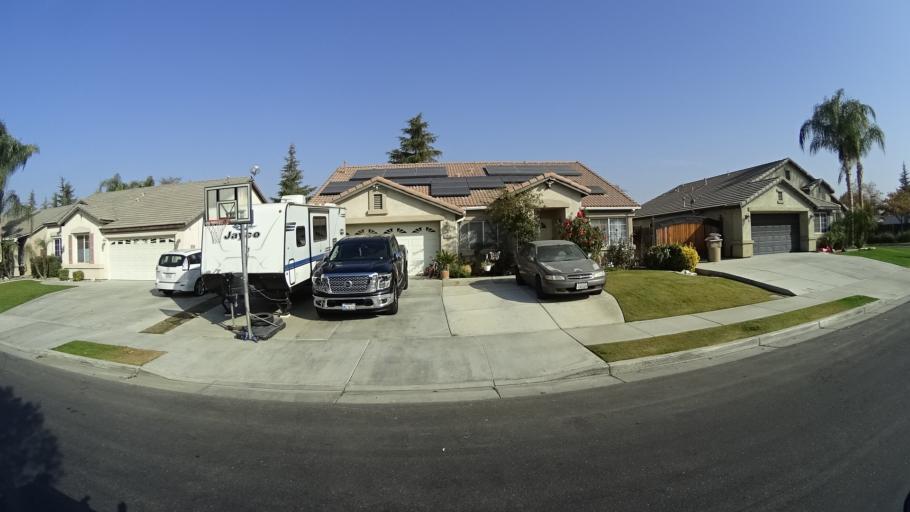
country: US
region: California
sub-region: Kern County
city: Greenacres
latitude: 35.4160
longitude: -119.1195
